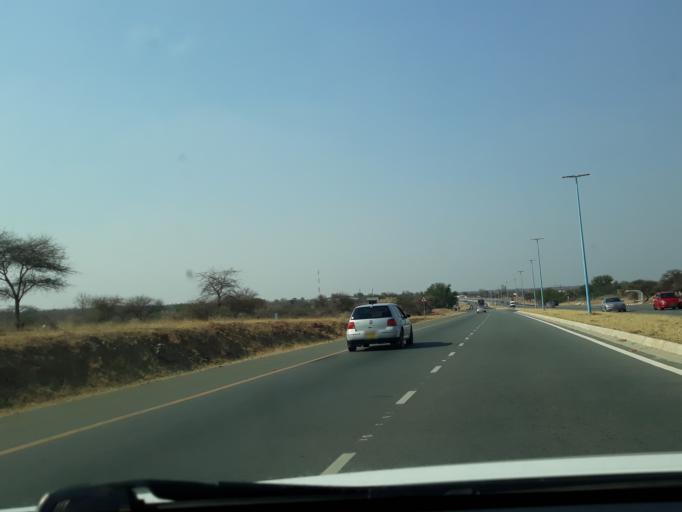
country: BW
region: Central
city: Tonota
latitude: -21.4124
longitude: 27.4496
